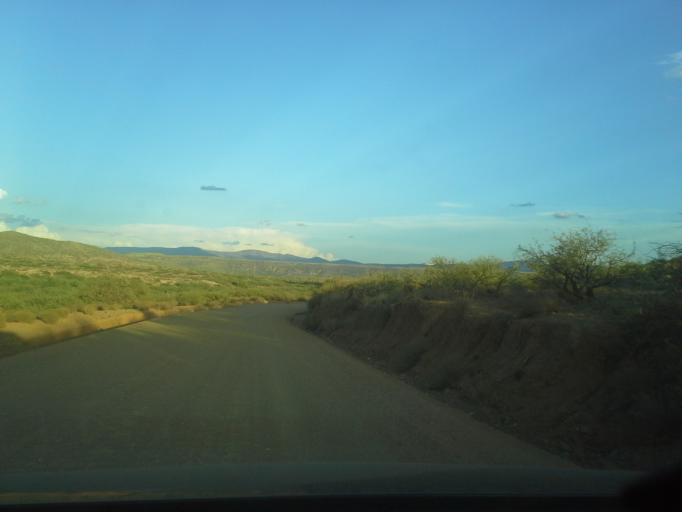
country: US
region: Arizona
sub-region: Yavapai County
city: Spring Valley
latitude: 34.2644
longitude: -112.1835
